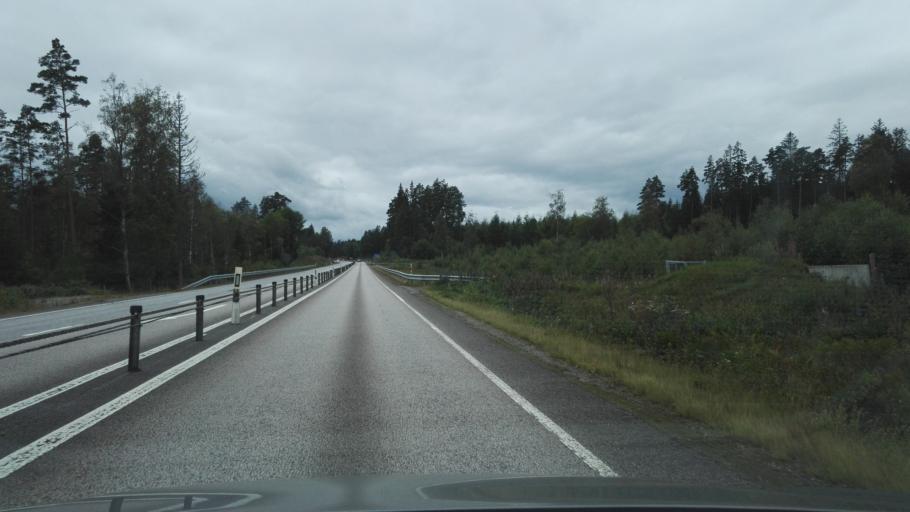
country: SE
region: Kronoberg
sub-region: Vaxjo Kommun
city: Braas
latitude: 56.9988
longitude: 15.0216
